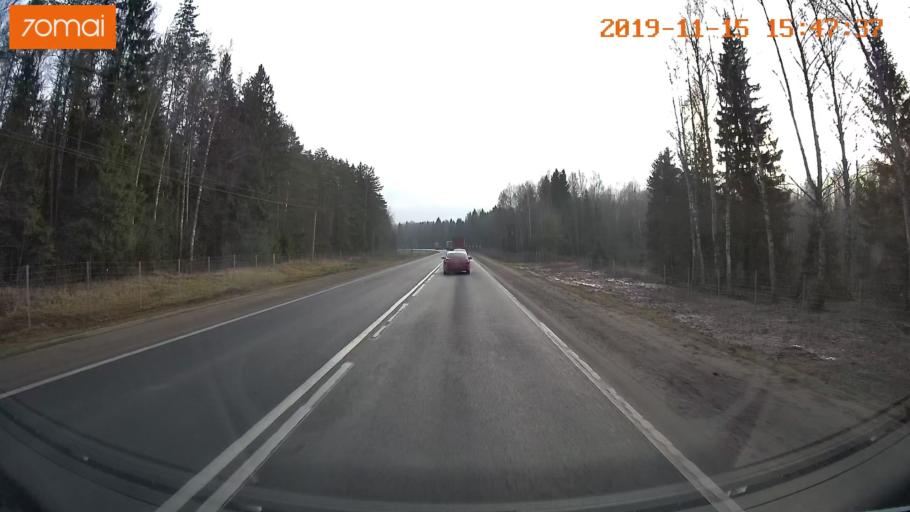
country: RU
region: Jaroslavl
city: Danilov
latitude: 57.9362
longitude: 40.0083
